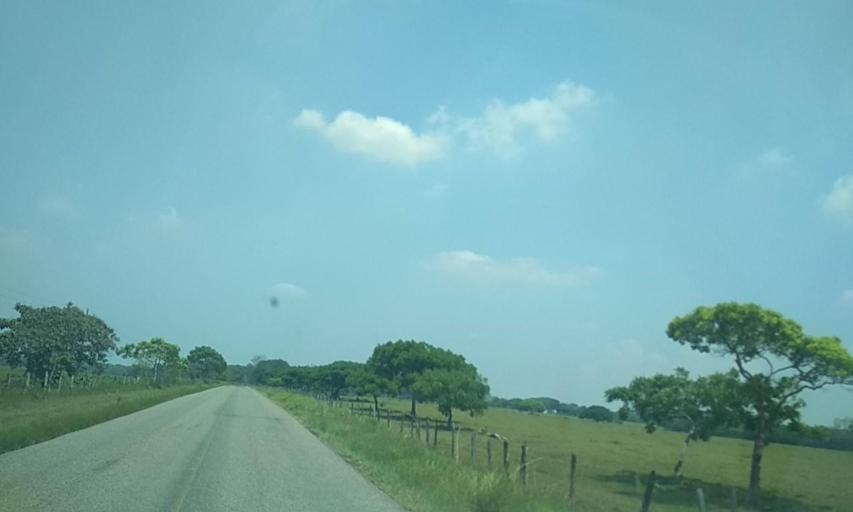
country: MX
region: Tabasco
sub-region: Cardenas
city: Poblado C-33 20 de Noviembre
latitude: 17.8524
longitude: -93.5756
